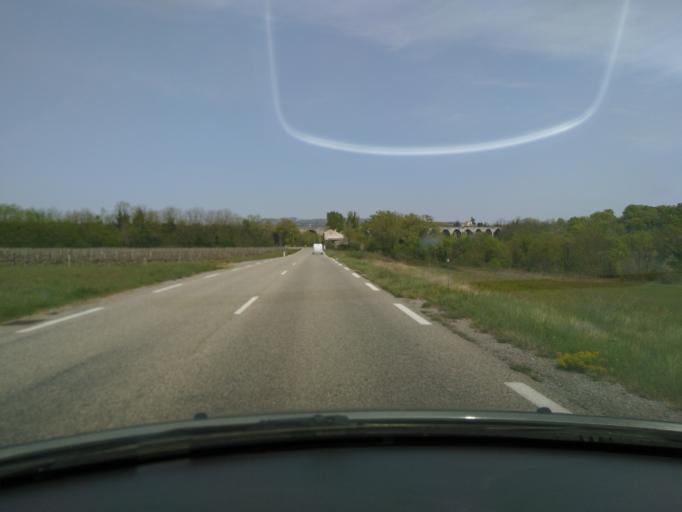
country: FR
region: Rhone-Alpes
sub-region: Departement de l'Ardeche
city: Lavilledieu
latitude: 44.5609
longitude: 4.4591
